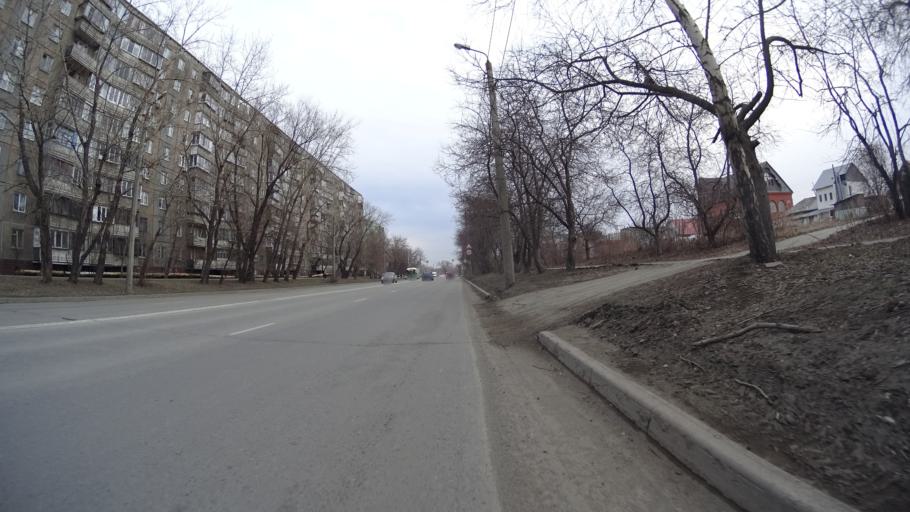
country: RU
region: Chelyabinsk
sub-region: Gorod Chelyabinsk
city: Chelyabinsk
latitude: 55.1900
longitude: 61.4812
